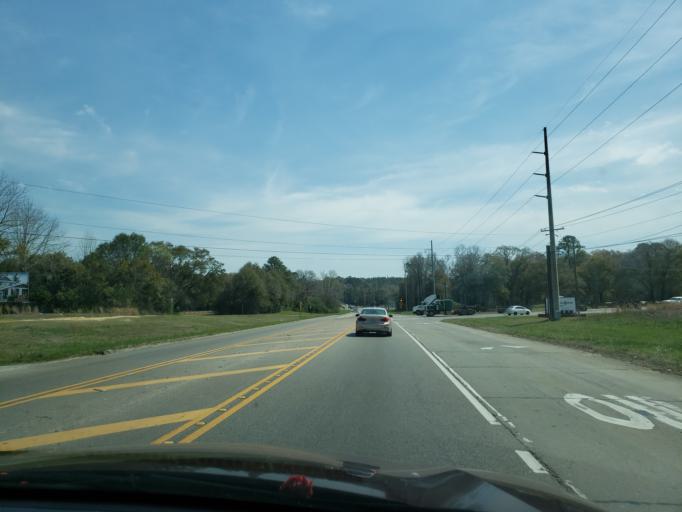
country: US
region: Alabama
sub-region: Autauga County
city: Prattville
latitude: 32.4368
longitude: -86.4689
